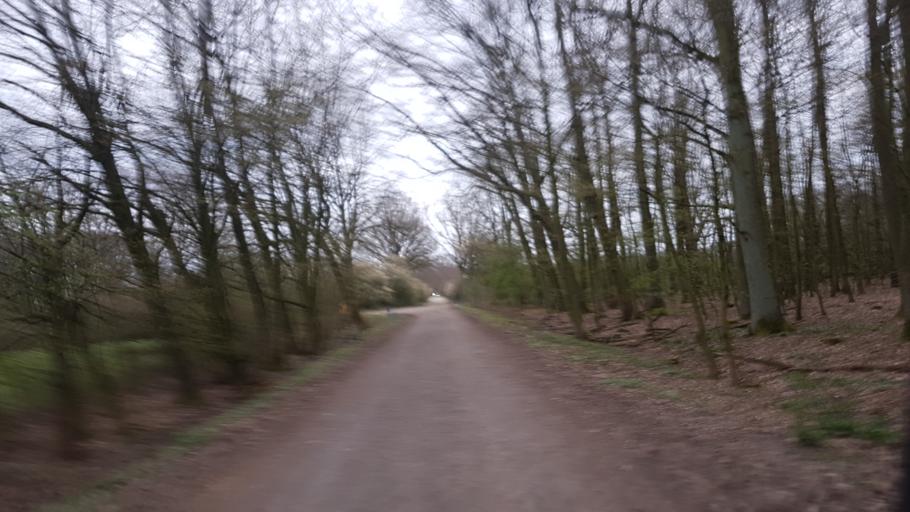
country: DE
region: Lower Saxony
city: Isernhagen Farster Bauerschaft
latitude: 52.4452
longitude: 9.8139
